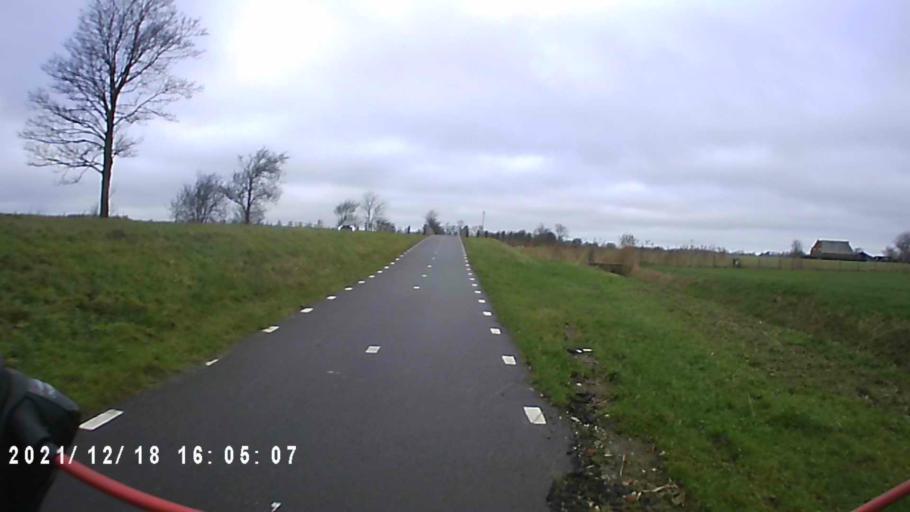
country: NL
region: Friesland
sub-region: Gemeente Dongeradeel
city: Anjum
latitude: 53.3531
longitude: 6.0771
